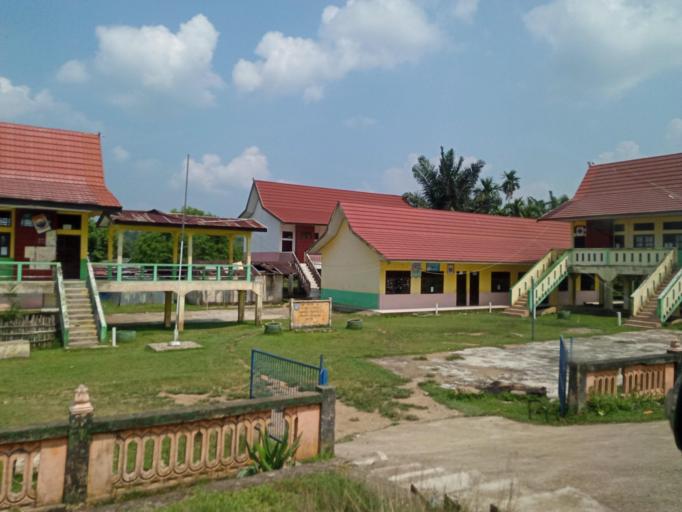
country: ID
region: Jambi
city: Mersam
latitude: -1.7062
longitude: 102.8828
